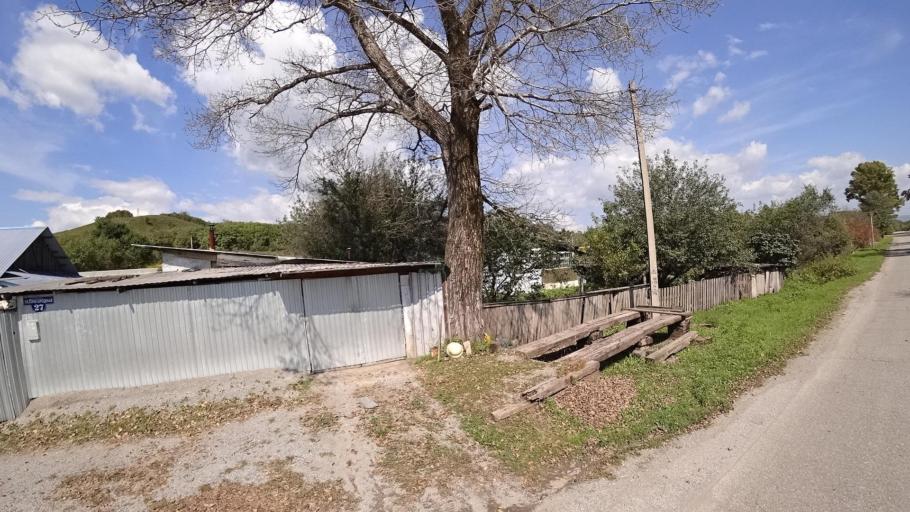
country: RU
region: Jewish Autonomous Oblast
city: Londoko
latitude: 49.0102
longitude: 131.9511
